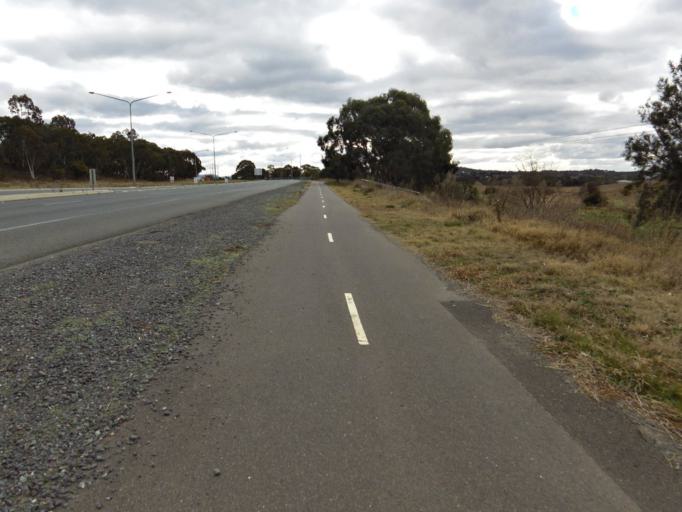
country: AU
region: Australian Capital Territory
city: Belconnen
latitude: -35.2331
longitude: 149.0867
